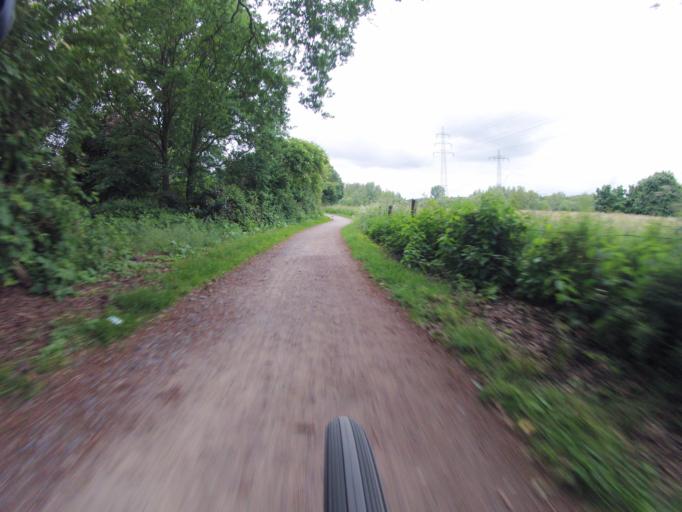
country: DE
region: North Rhine-Westphalia
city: Emsdetten
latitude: 52.1789
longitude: 7.5442
